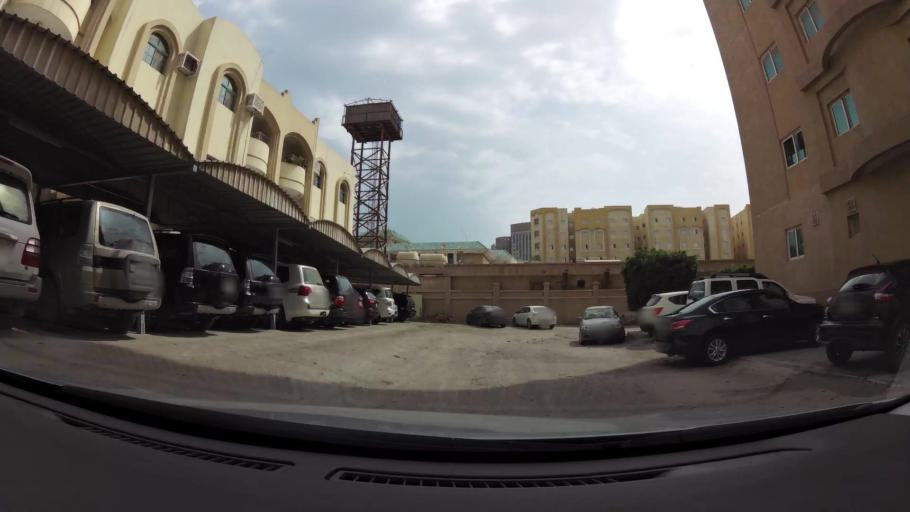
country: QA
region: Baladiyat ad Dawhah
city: Doha
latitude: 25.2856
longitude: 51.5001
